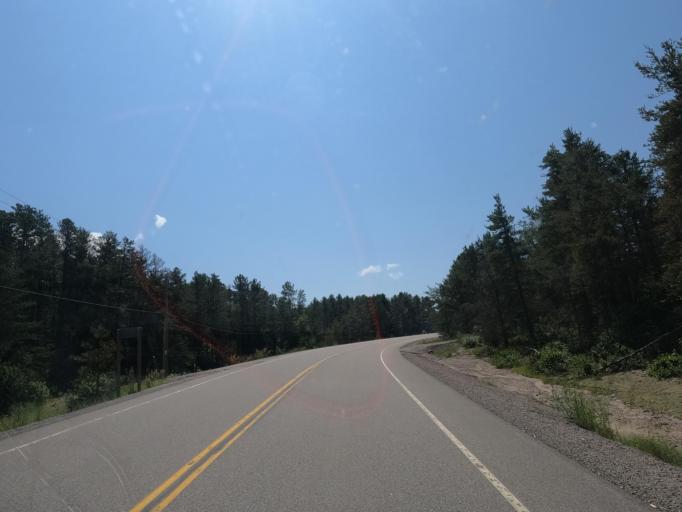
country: CA
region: Ontario
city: Dryden
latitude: 49.8563
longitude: -93.3635
